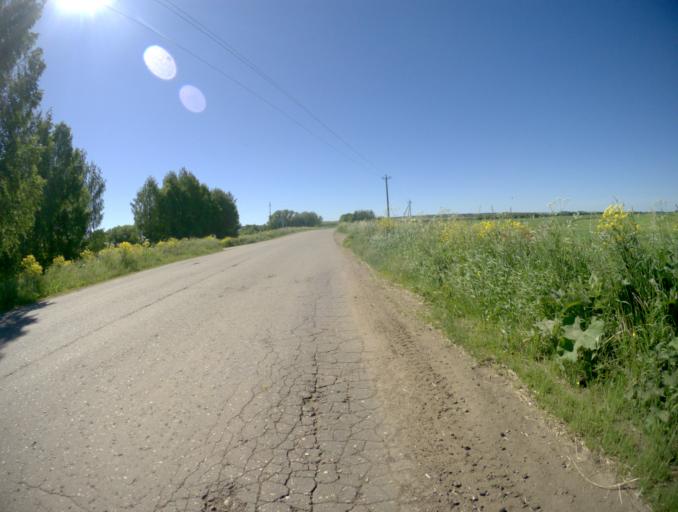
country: RU
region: Vladimir
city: Yur'yev-Pol'skiy
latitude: 56.6107
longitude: 39.8739
